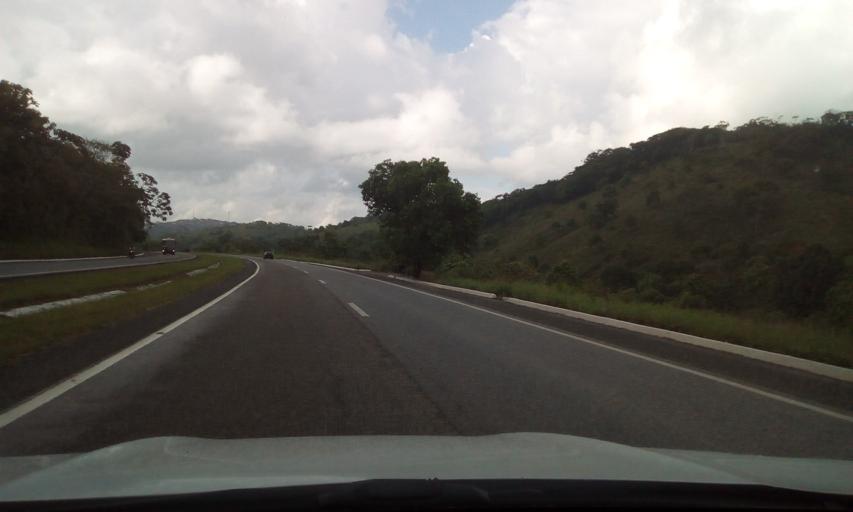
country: BR
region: Pernambuco
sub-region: Cabo De Santo Agostinho
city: Cabo
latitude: -8.2680
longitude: -35.0530
